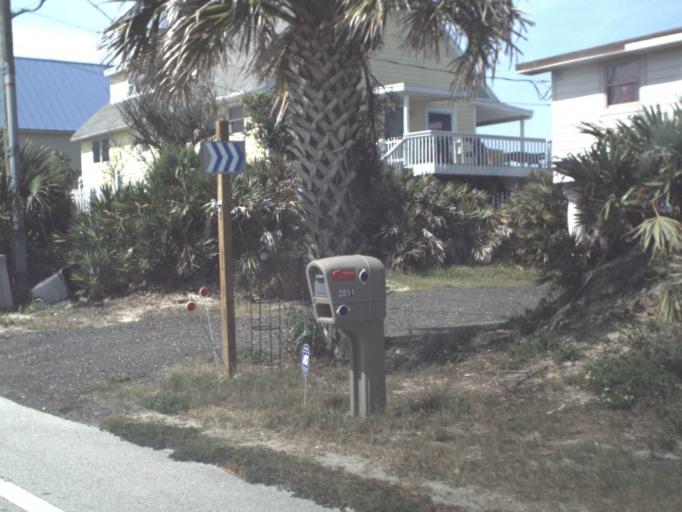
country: US
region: Florida
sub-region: Saint Johns County
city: Villano Beach
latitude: 30.0060
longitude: -81.3191
